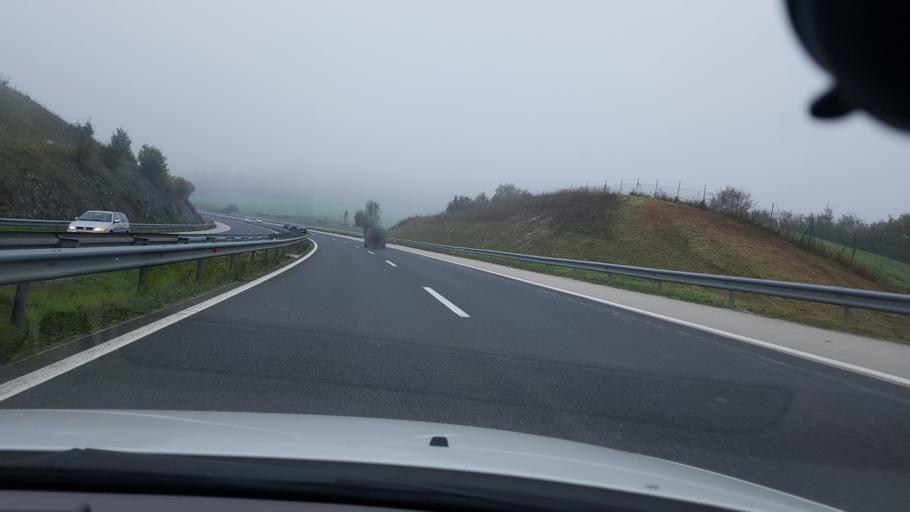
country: SI
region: Trebnje
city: Trebnje
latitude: 45.9189
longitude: 14.9527
